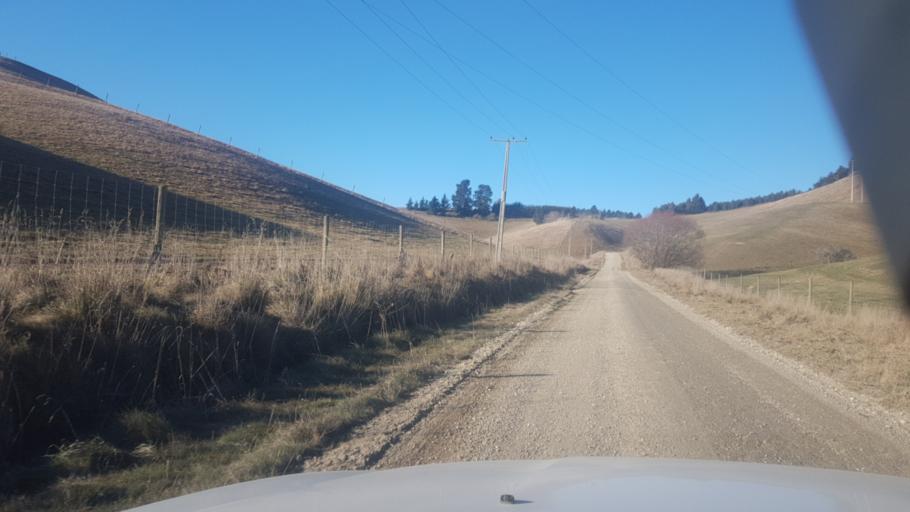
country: NZ
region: Canterbury
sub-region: Timaru District
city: Pleasant Point
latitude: -44.3432
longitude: 171.0629
